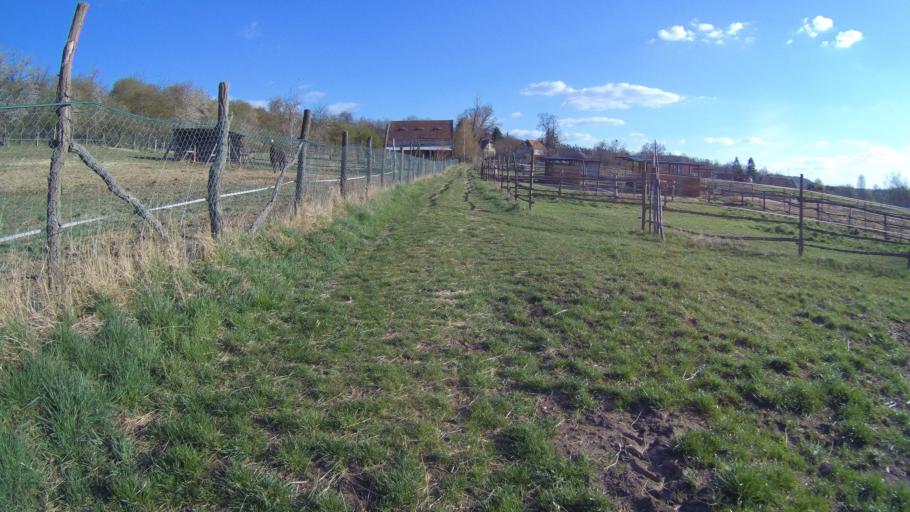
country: CZ
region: Ustecky
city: Zatec
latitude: 50.2928
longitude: 13.5765
